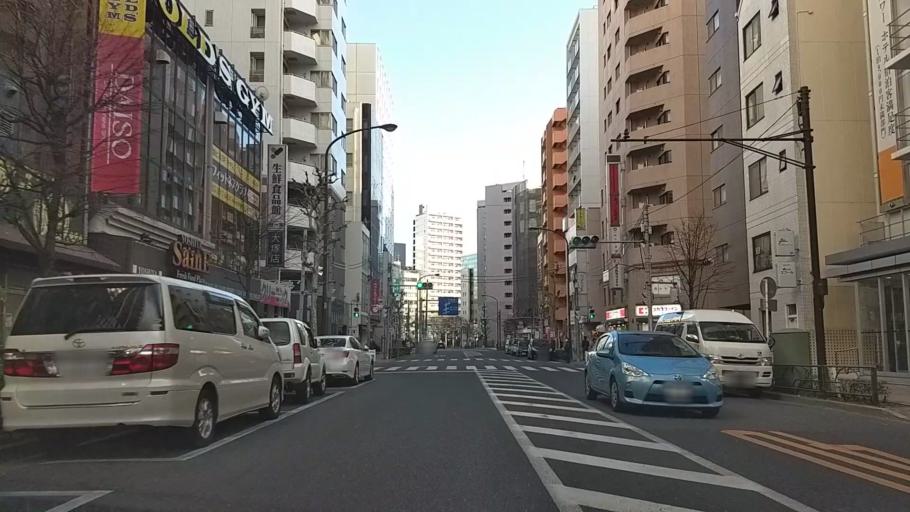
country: JP
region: Tokyo
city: Tokyo
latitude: 35.7339
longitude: 139.7280
